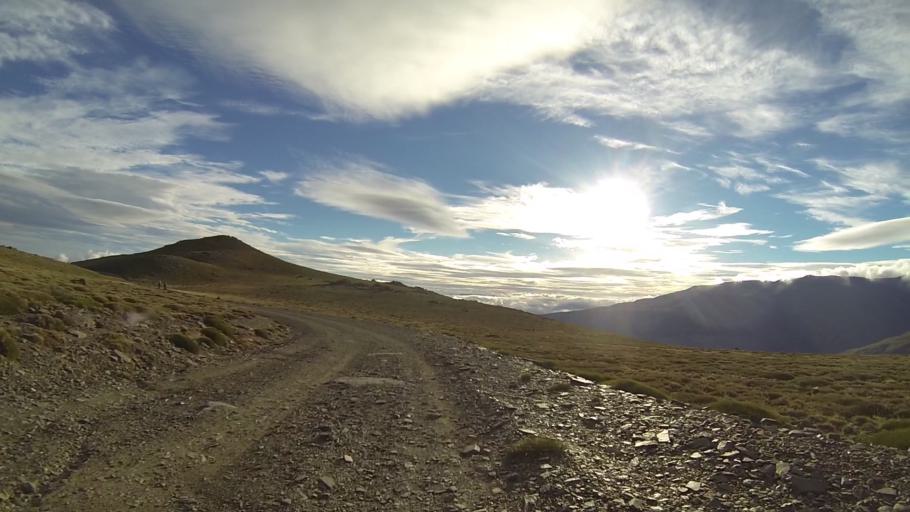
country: ES
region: Andalusia
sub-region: Provincia de Granada
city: Trevelez
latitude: 36.9984
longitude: -3.3116
